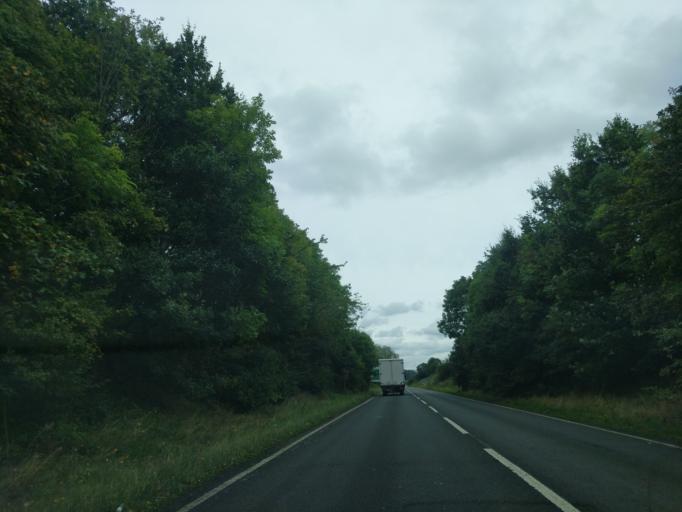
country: GB
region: England
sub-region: Cheshire East
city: Weston
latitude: 53.0655
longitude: -2.3871
